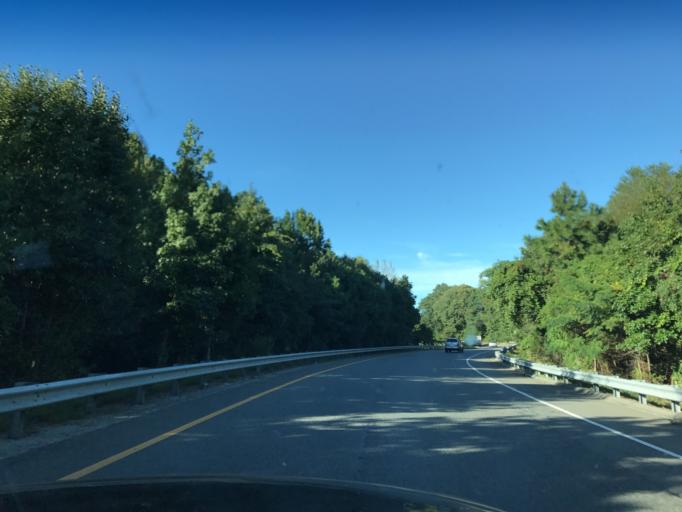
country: US
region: Virginia
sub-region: City of Chesapeake
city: Chesapeake
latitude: 36.7608
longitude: -76.2664
